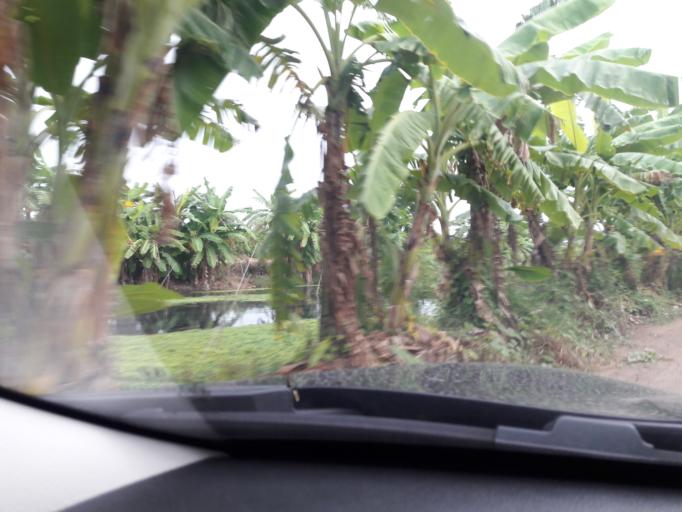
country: TH
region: Ratchaburi
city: Bang Phae
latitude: 13.6261
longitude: 99.9628
